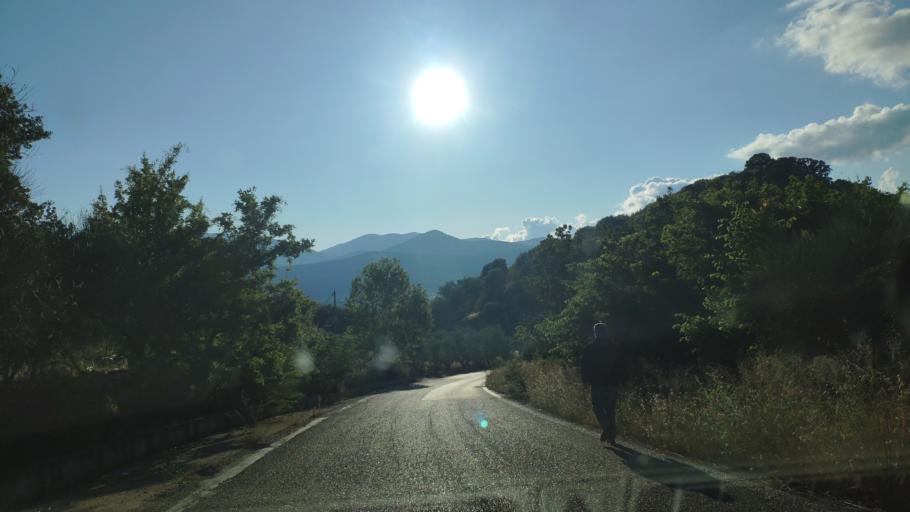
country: GR
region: West Greece
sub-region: Nomos Aitolias kai Akarnanias
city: Fitiai
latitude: 38.6422
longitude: 21.1883
